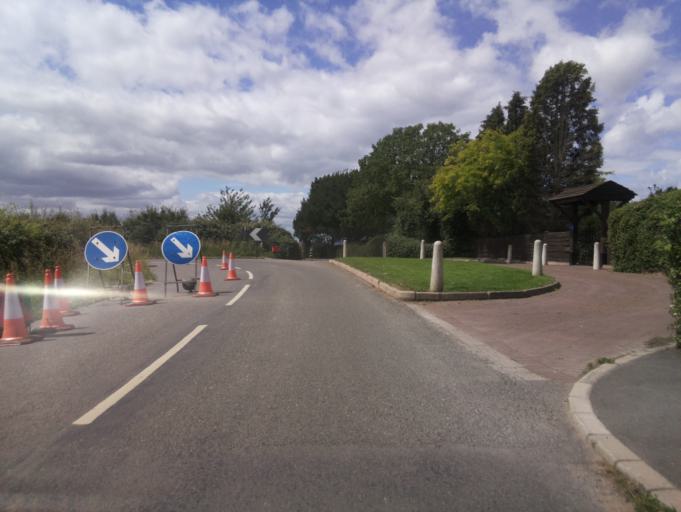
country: GB
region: England
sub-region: Nottinghamshire
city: Ruddington
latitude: 52.8677
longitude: -1.0922
